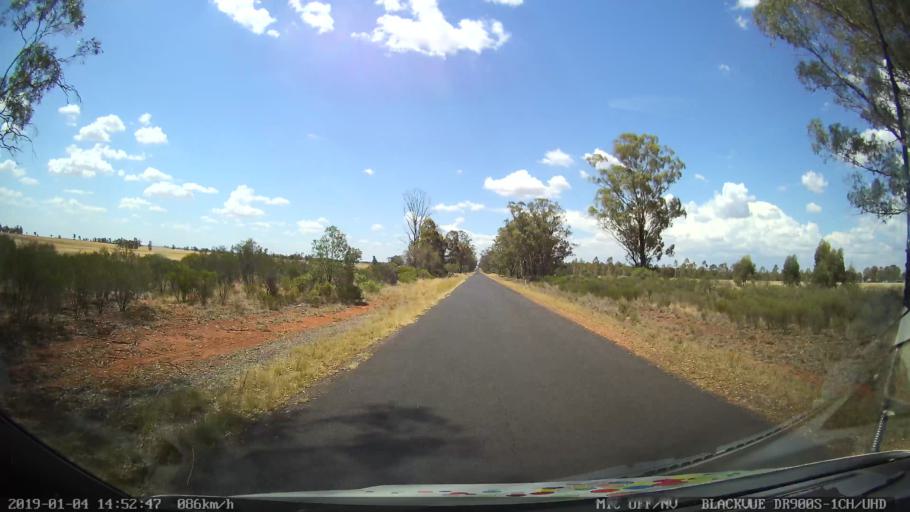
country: AU
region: New South Wales
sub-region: Dubbo Municipality
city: Dubbo
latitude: -32.0113
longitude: 148.6506
